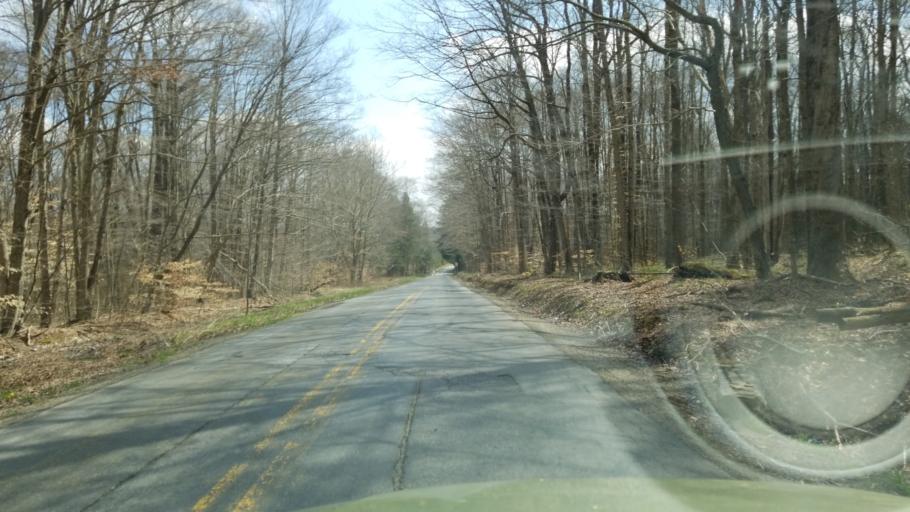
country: US
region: Pennsylvania
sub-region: Jefferson County
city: Brockway
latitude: 41.2786
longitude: -78.8554
